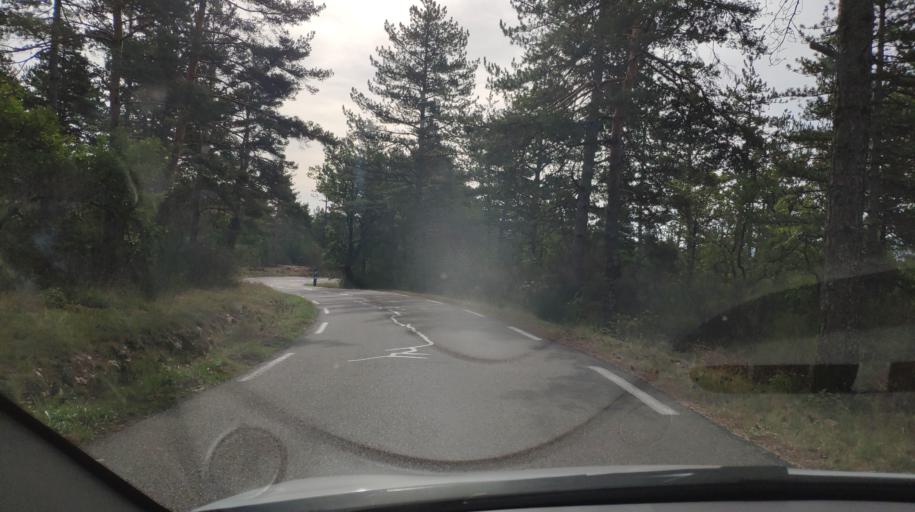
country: FR
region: Provence-Alpes-Cote d'Azur
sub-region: Departement du Vaucluse
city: Sault
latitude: 44.1192
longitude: 5.3812
